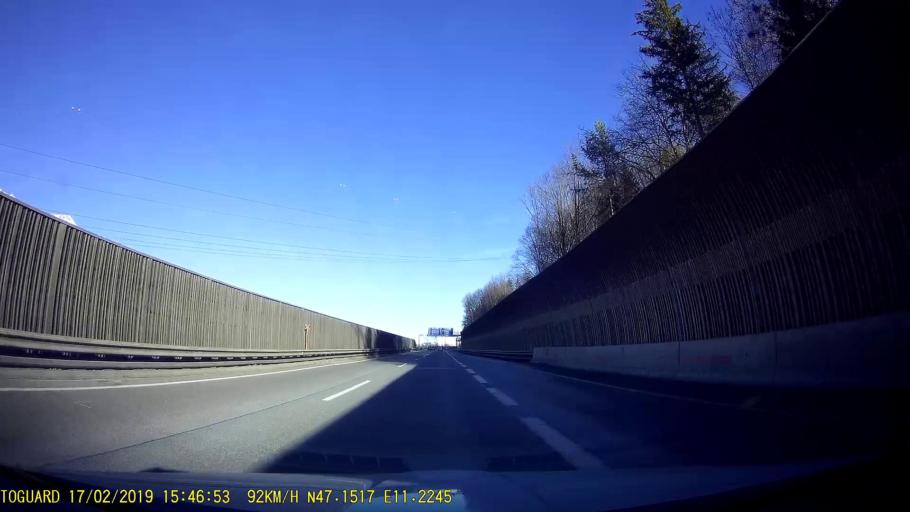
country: AT
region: Tyrol
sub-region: Politischer Bezirk Innsbruck Land
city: Natters
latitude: 47.2527
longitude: 11.3742
